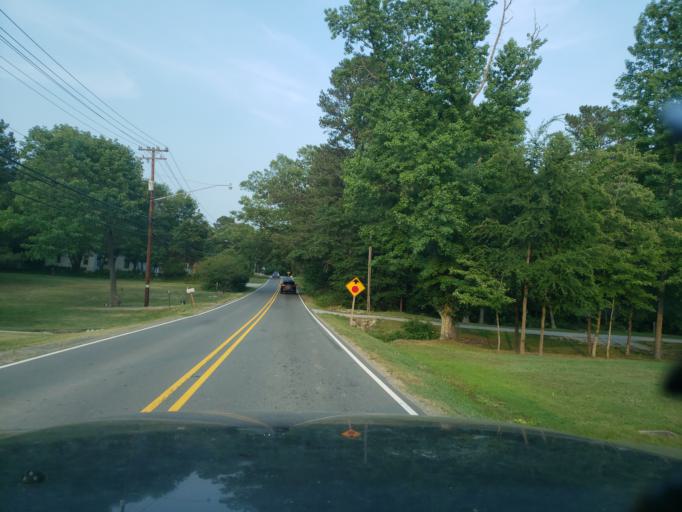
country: US
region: North Carolina
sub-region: Durham County
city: Durham
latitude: 35.9579
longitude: -78.8748
